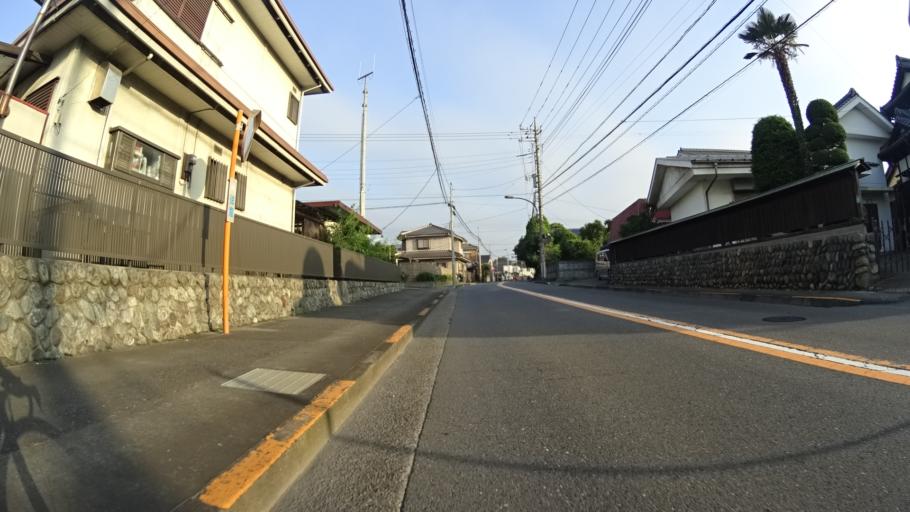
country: JP
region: Tokyo
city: Fussa
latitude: 35.7626
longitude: 139.3018
